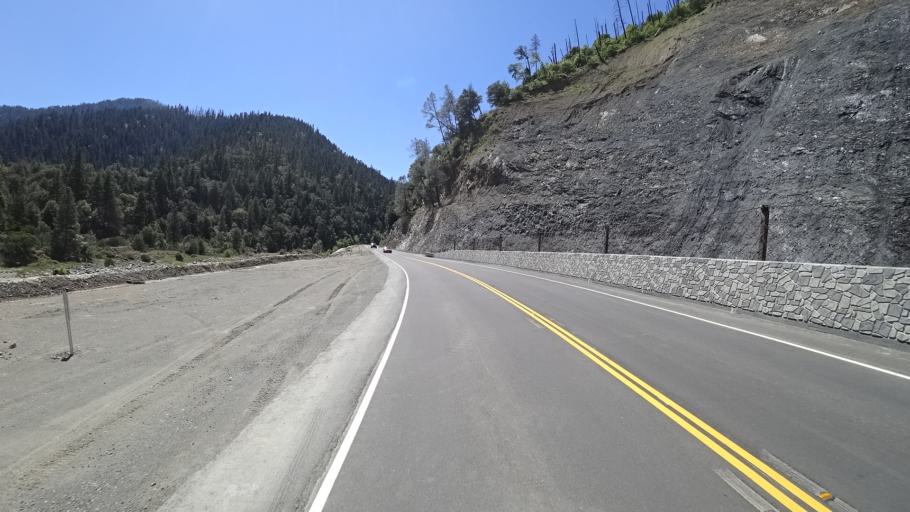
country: US
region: California
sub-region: Trinity County
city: Hayfork
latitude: 40.7798
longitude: -123.3110
